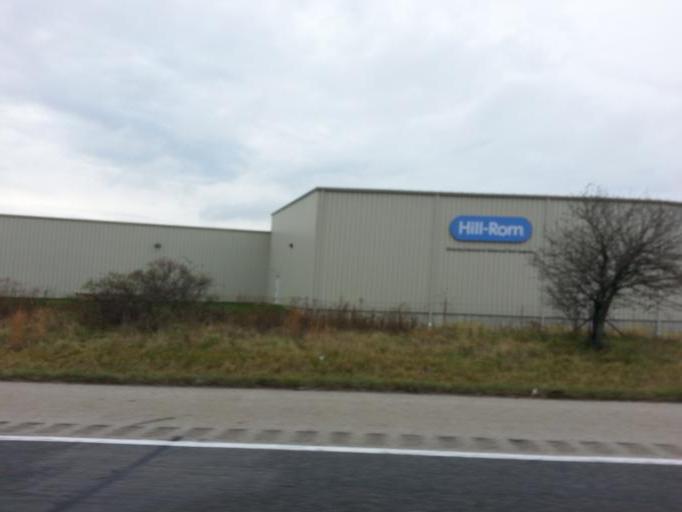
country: US
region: Indiana
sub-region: Ripley County
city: Batesville
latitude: 39.2953
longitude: -85.1805
